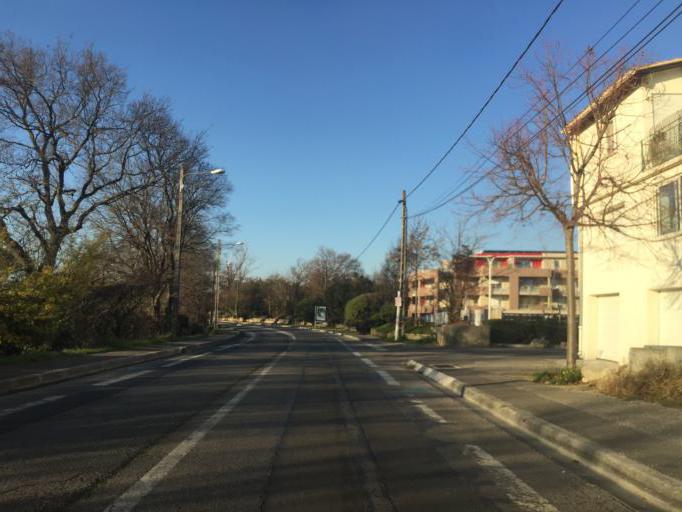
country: FR
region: Provence-Alpes-Cote d'Azur
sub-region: Departement du Vaucluse
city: Montfavet
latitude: 43.9389
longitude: 4.8704
